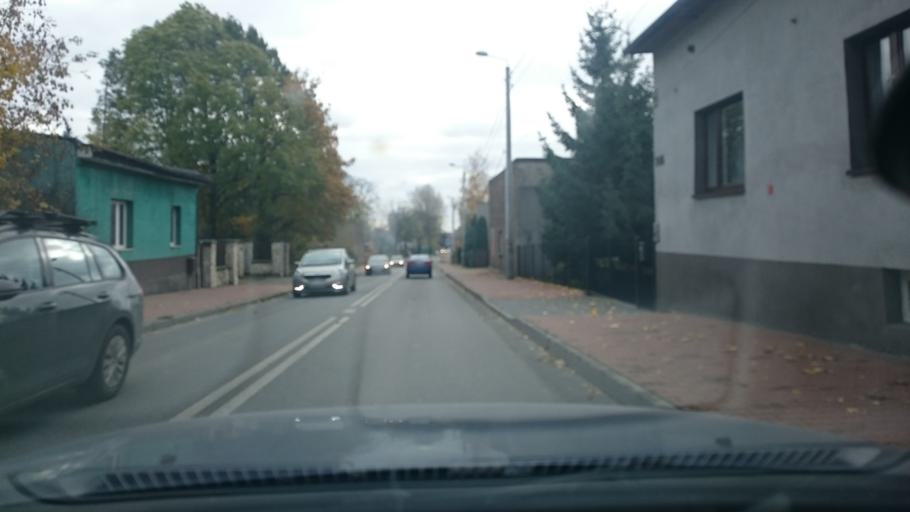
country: PL
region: Silesian Voivodeship
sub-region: Powiat bedzinski
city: Bedzin
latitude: 50.3472
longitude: 19.0991
